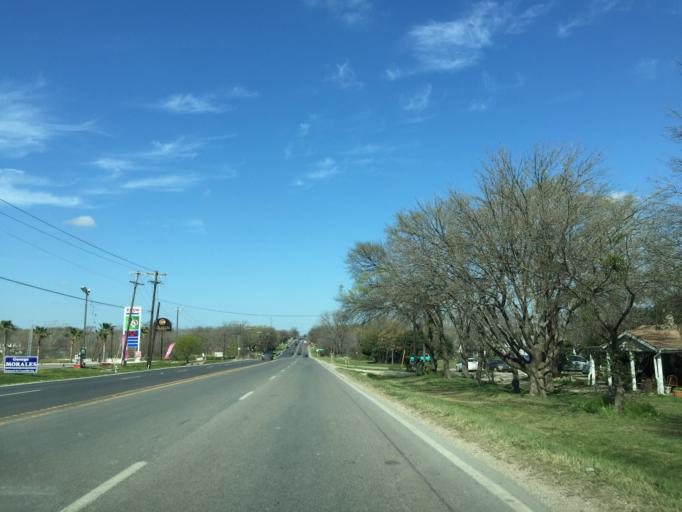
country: US
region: Texas
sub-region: Travis County
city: Onion Creek
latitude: 30.1611
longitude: -97.6862
